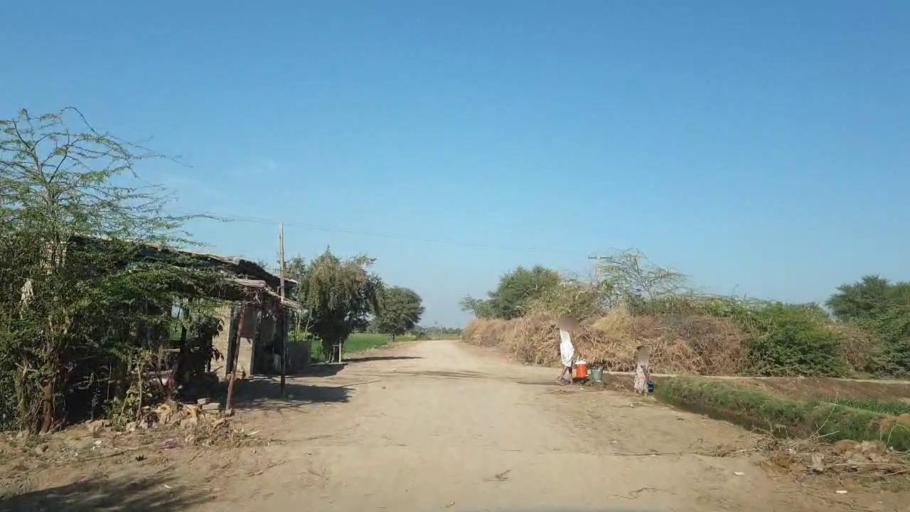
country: PK
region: Sindh
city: Tando Adam
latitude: 25.6774
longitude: 68.6869
